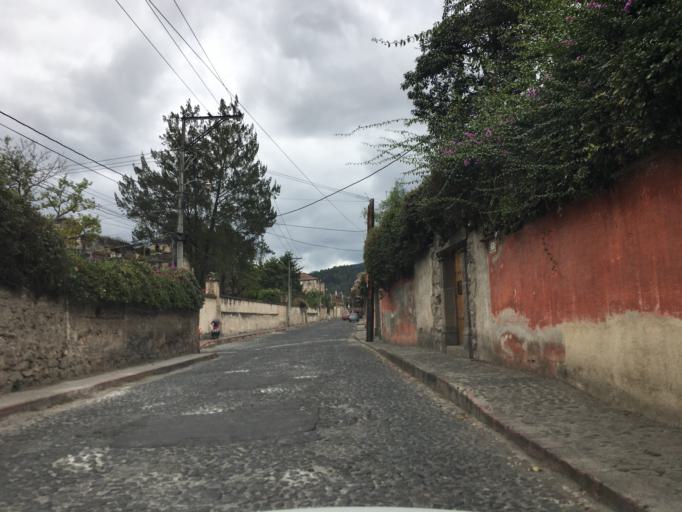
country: GT
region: Sacatepequez
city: Antigua Guatemala
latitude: 14.5522
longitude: -90.7288
